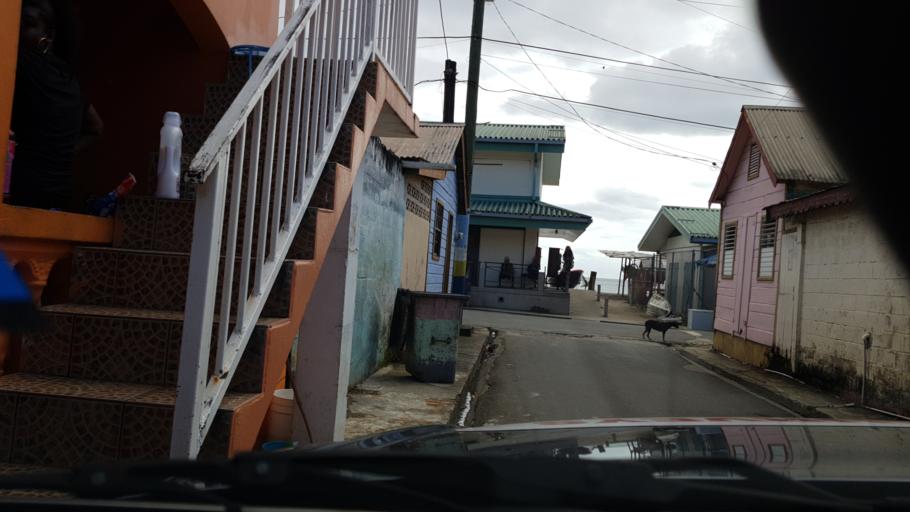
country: LC
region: Anse-la-Raye
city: Anse La Raye
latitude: 13.9411
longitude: -61.0430
